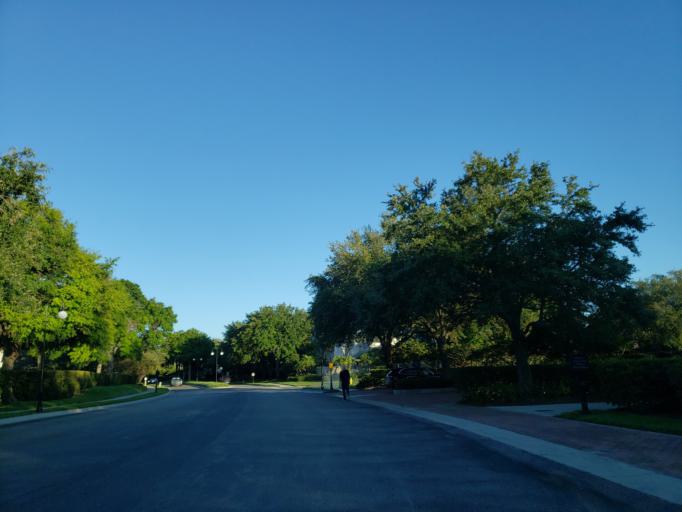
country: US
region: Florida
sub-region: Hillsborough County
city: Tampa
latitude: 27.9361
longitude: -82.4527
